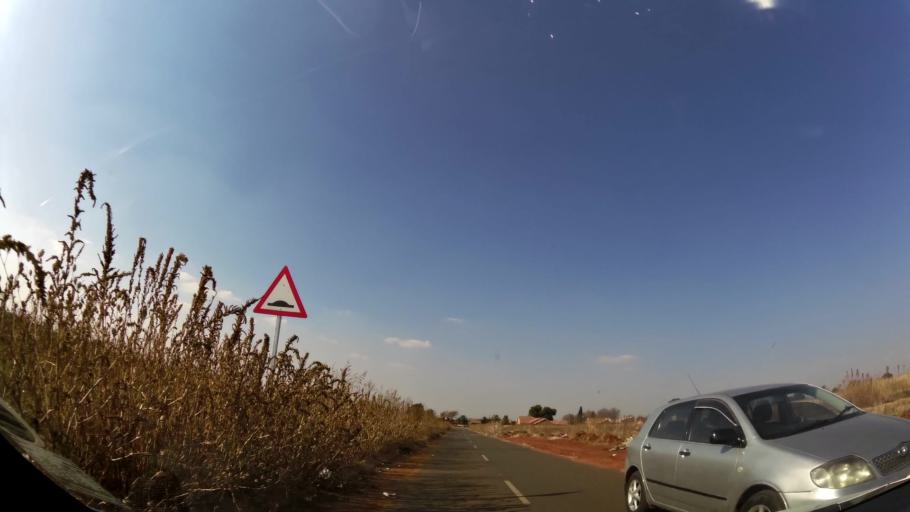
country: ZA
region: Gauteng
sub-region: Ekurhuleni Metropolitan Municipality
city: Brakpan
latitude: -26.2299
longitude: 28.3304
